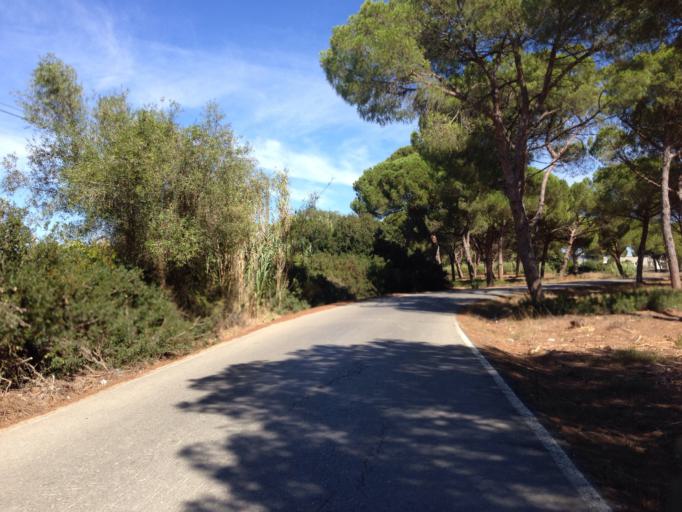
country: ES
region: Andalusia
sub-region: Provincia de Cadiz
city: Conil de la Frontera
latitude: 36.3227
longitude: -6.1328
